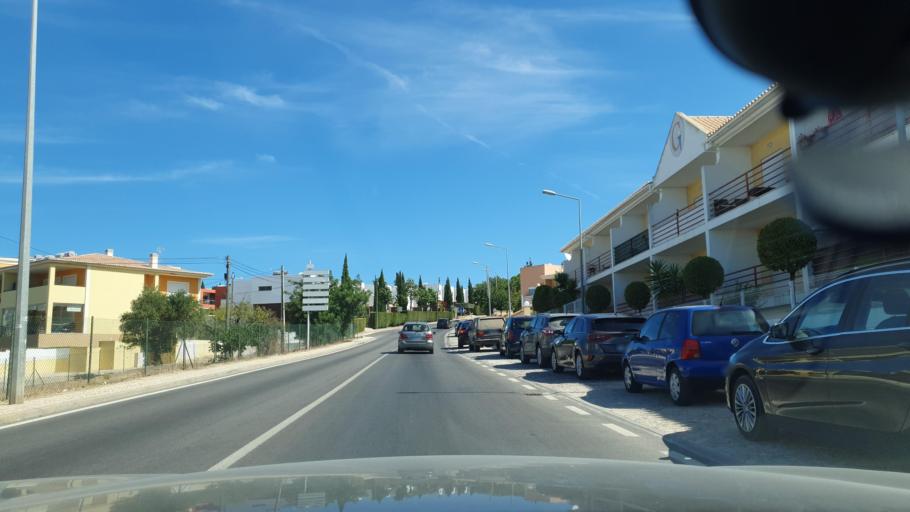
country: PT
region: Faro
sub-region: Albufeira
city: Guia
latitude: 37.0975
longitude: -8.3094
